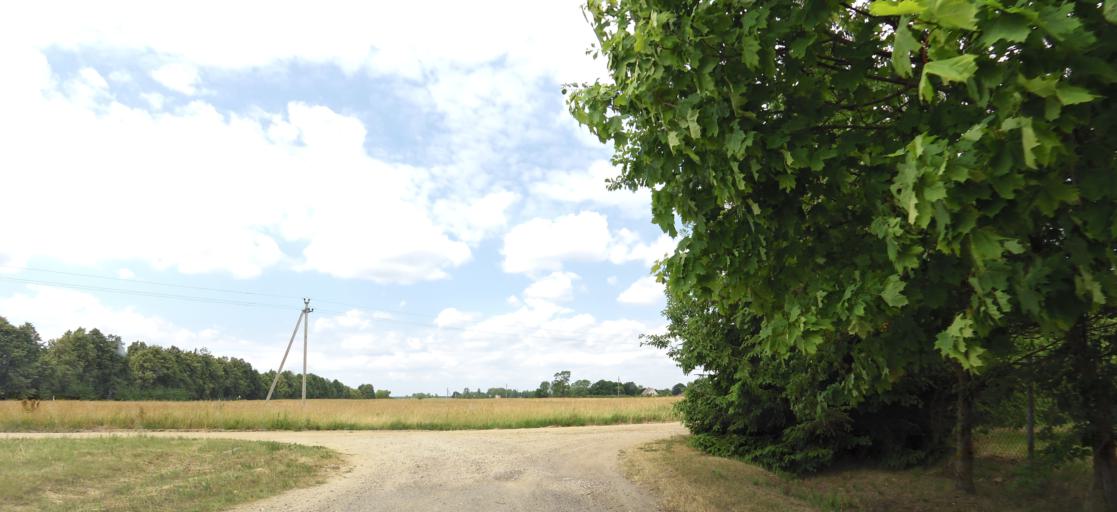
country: LT
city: Sirvintos
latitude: 55.0550
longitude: 24.9204
